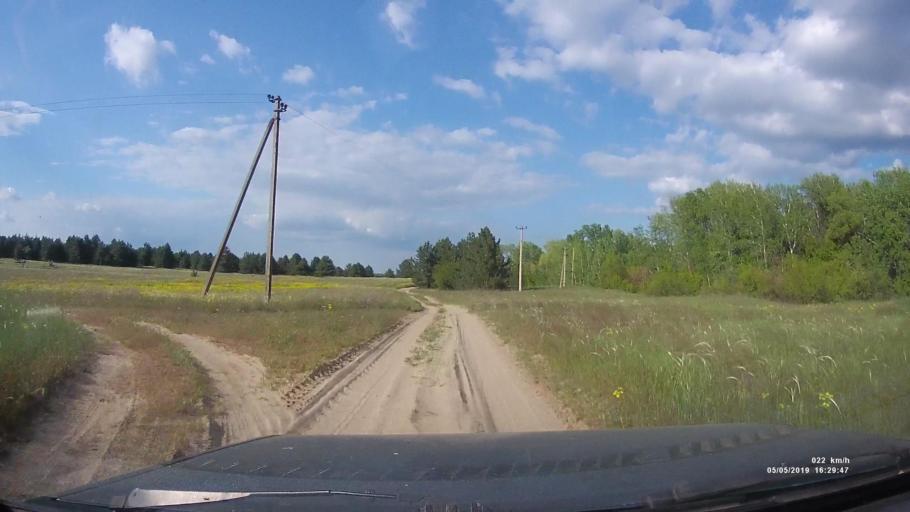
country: RU
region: Rostov
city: Ust'-Donetskiy
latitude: 47.7715
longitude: 41.0146
